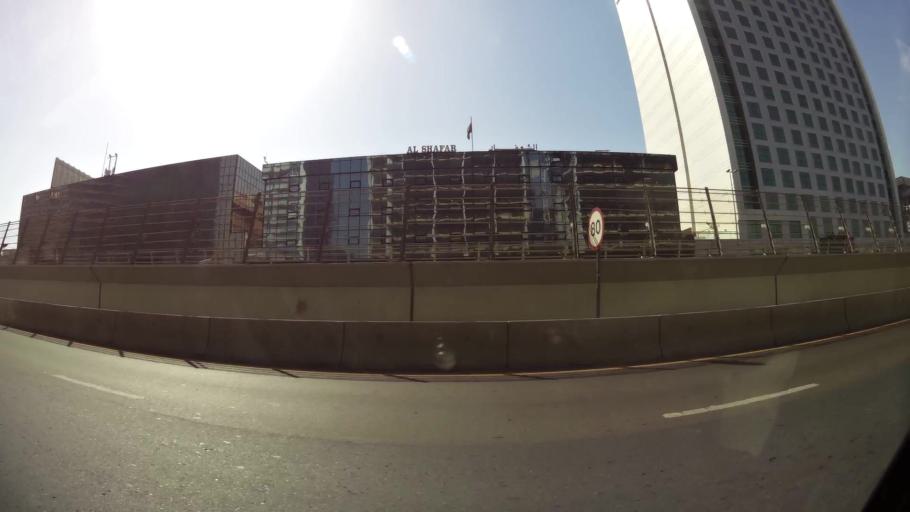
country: AE
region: Ash Shariqah
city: Sharjah
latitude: 25.2499
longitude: 55.3013
